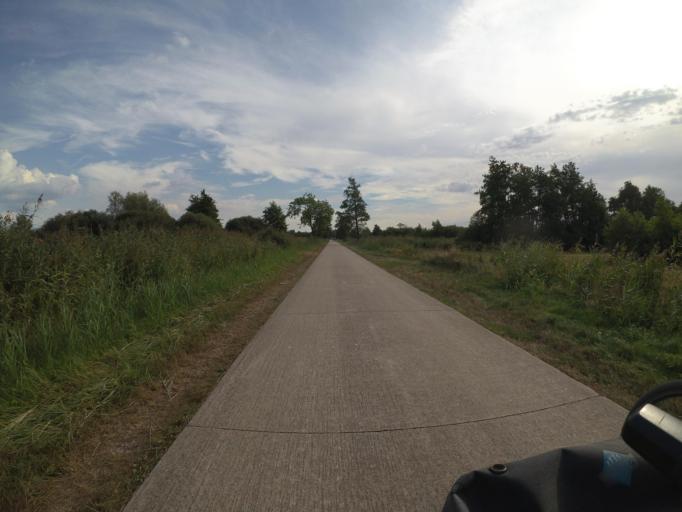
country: NL
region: Overijssel
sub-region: Gemeente Zwartewaterland
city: Hasselt
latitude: 52.6312
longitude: 6.1034
